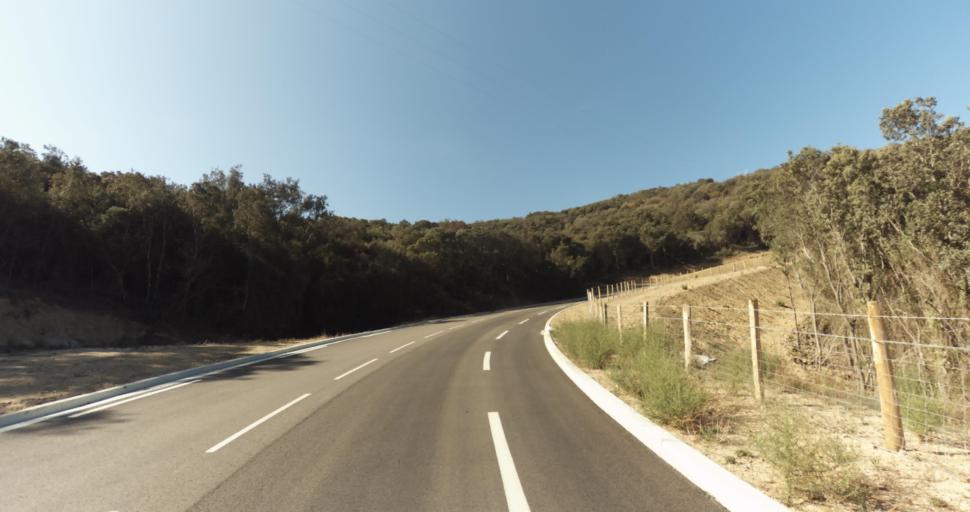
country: FR
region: Corsica
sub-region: Departement de la Corse-du-Sud
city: Ajaccio
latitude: 41.9244
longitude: 8.6475
